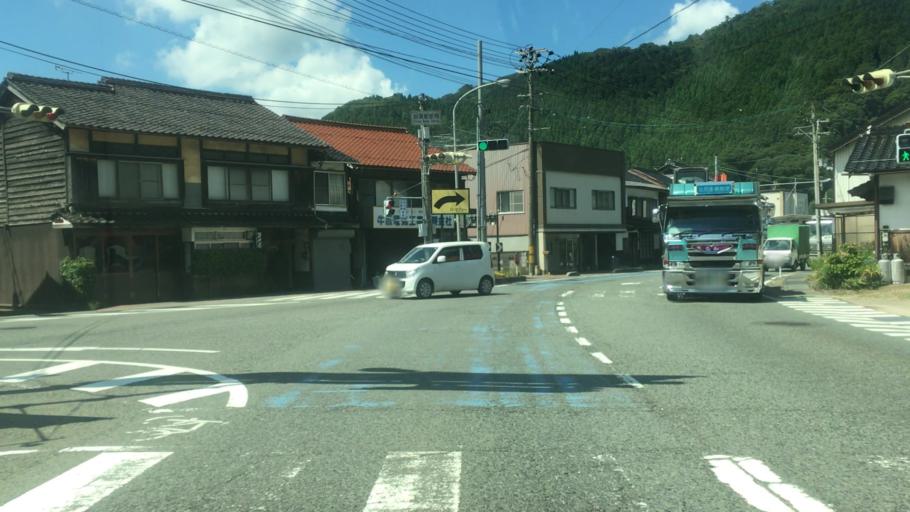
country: JP
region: Tottori
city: Tottori
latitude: 35.2662
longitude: 134.2288
